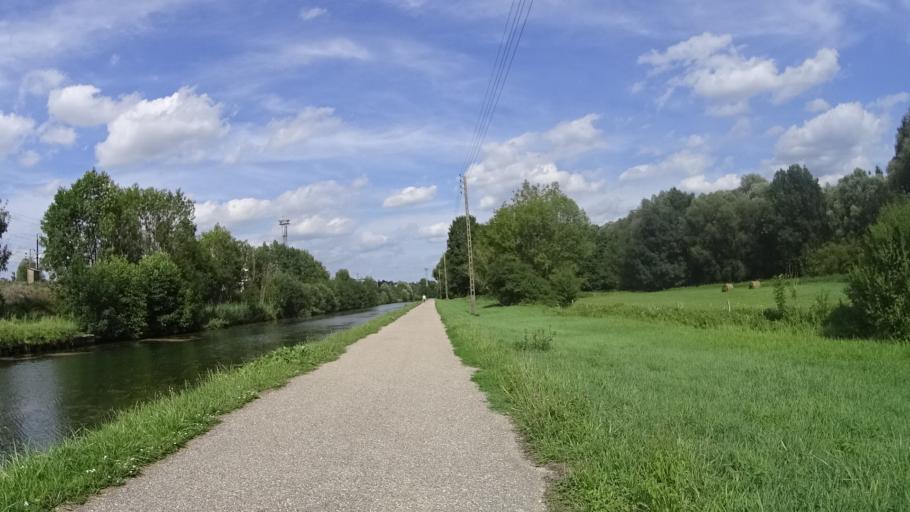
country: FR
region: Lorraine
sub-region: Departement de Meurthe-et-Moselle
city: Ecrouves
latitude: 48.6755
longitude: 5.8644
